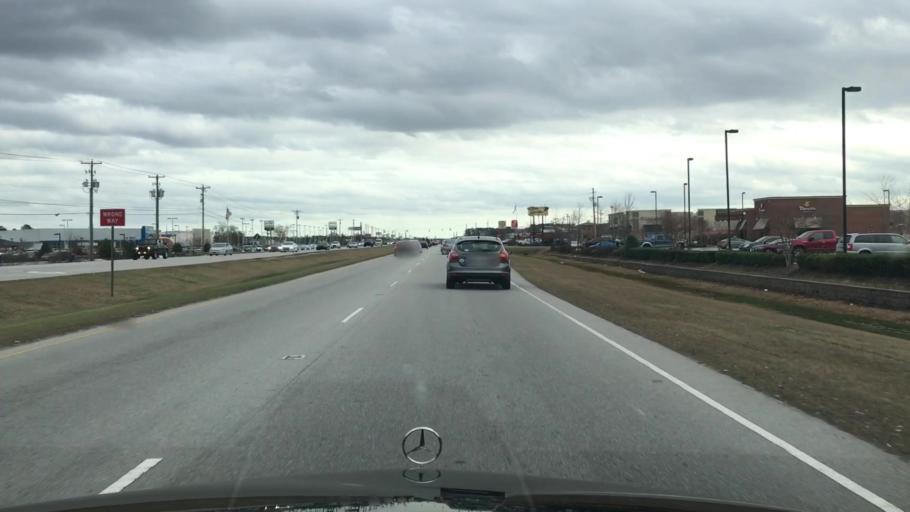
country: US
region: North Carolina
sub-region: Onslow County
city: Pumpkin Center
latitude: 34.7908
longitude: -77.4057
